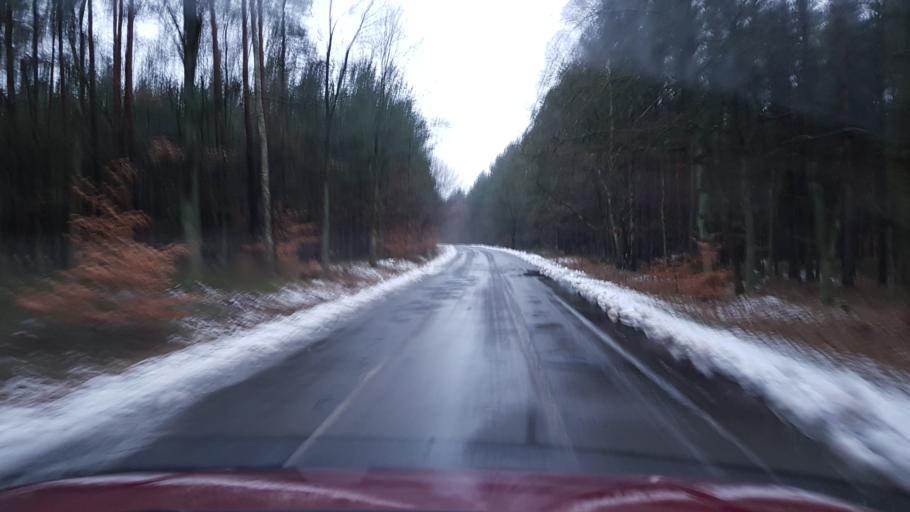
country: PL
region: West Pomeranian Voivodeship
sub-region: Powiat goleniowski
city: Goleniow
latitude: 53.4949
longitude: 14.8789
